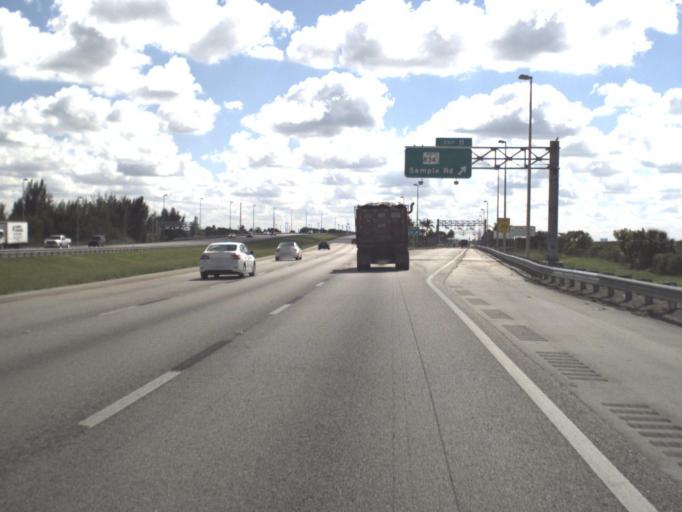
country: US
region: Florida
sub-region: Broward County
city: Coral Springs
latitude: 26.2788
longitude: -80.2973
